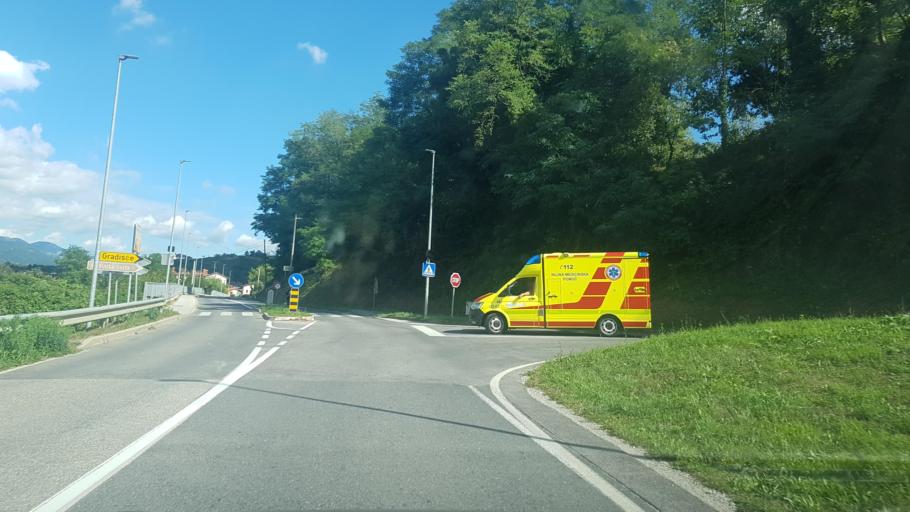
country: SI
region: Nova Gorica
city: Prvacina
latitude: 45.8851
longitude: 13.7279
